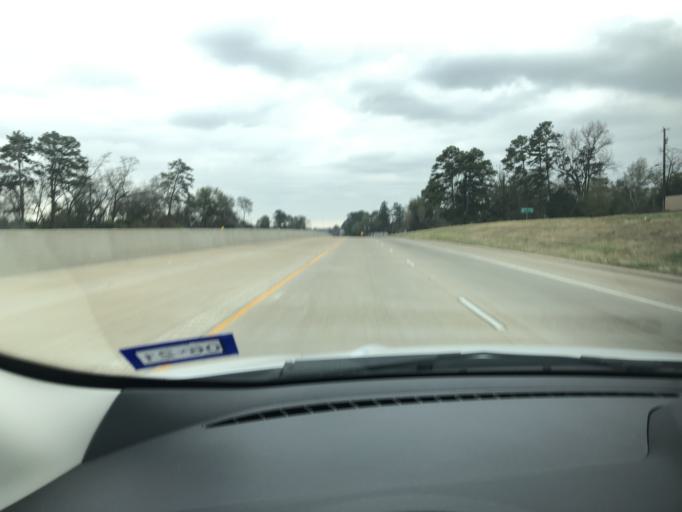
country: US
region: Texas
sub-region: Angelina County
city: Redland
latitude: 31.4070
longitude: -94.7203
